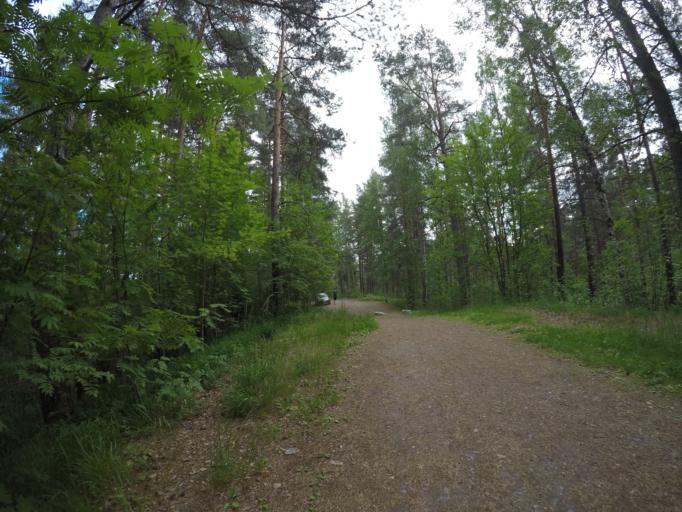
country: FI
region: Haeme
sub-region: Haemeenlinna
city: Haemeenlinna
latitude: 60.9912
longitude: 24.4250
